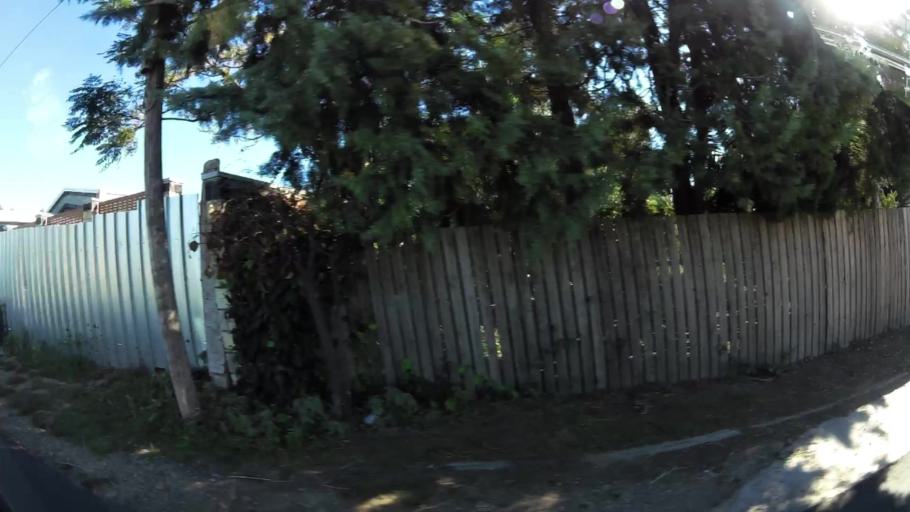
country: GR
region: Attica
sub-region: Nomarchia Anatolikis Attikis
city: Varybobi
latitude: 38.1145
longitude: 23.7898
